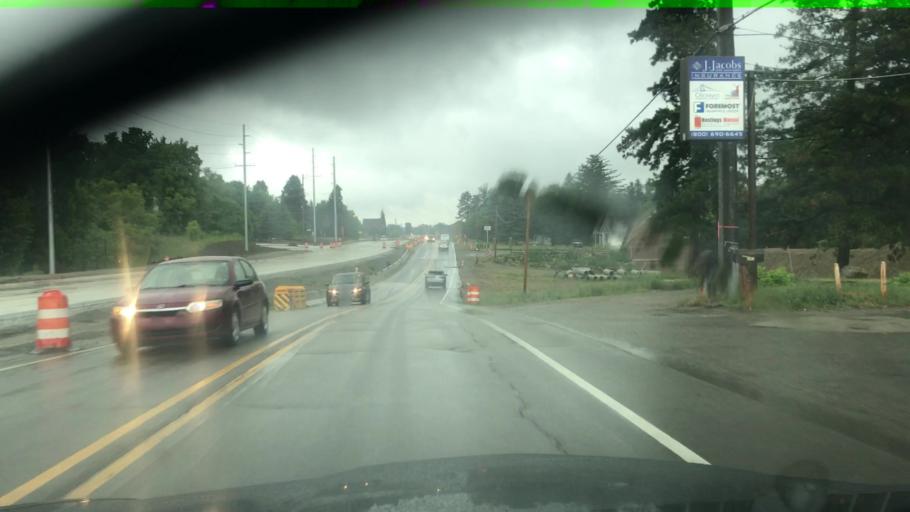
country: US
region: Michigan
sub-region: Oakland County
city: Auburn Hills
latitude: 42.7171
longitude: -83.3073
